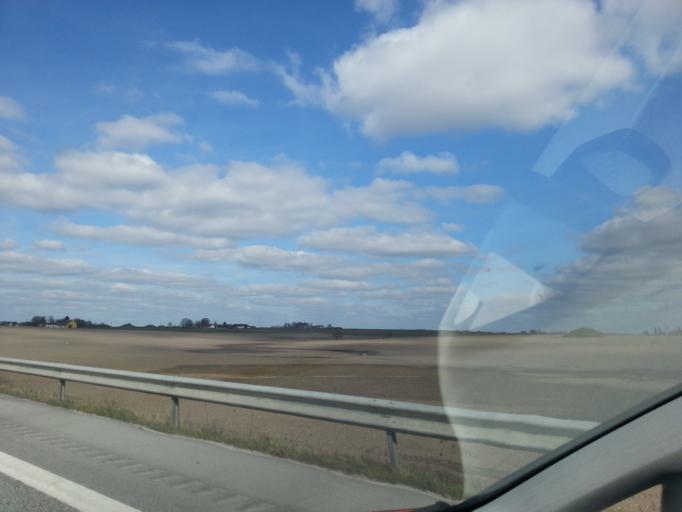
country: SE
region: Skane
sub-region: Malmo
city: Tygelsjo
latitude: 55.5045
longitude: 13.0182
